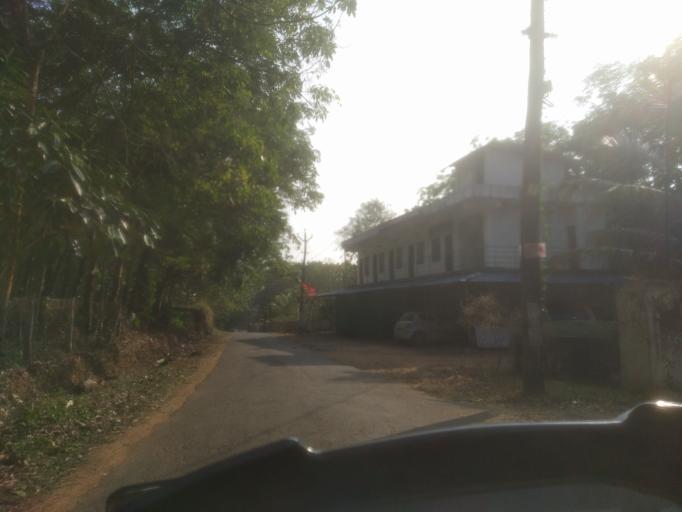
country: IN
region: Kerala
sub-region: Ernakulam
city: Piravam
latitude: 9.8420
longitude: 76.5255
